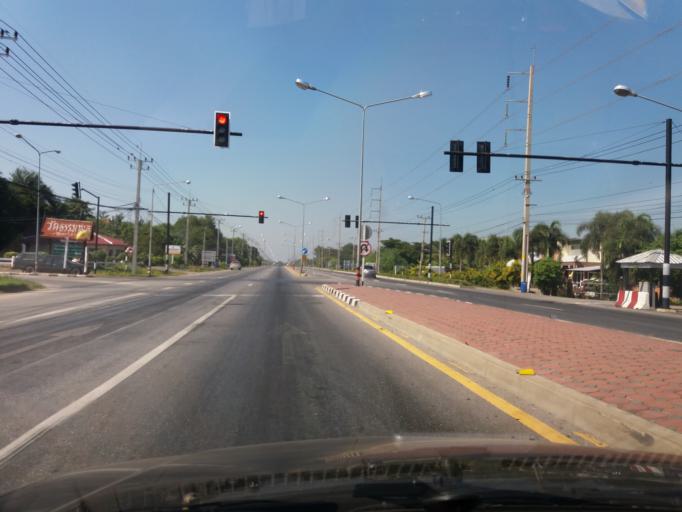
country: TH
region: Chai Nat
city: Wat Sing
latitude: 15.2507
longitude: 100.0980
